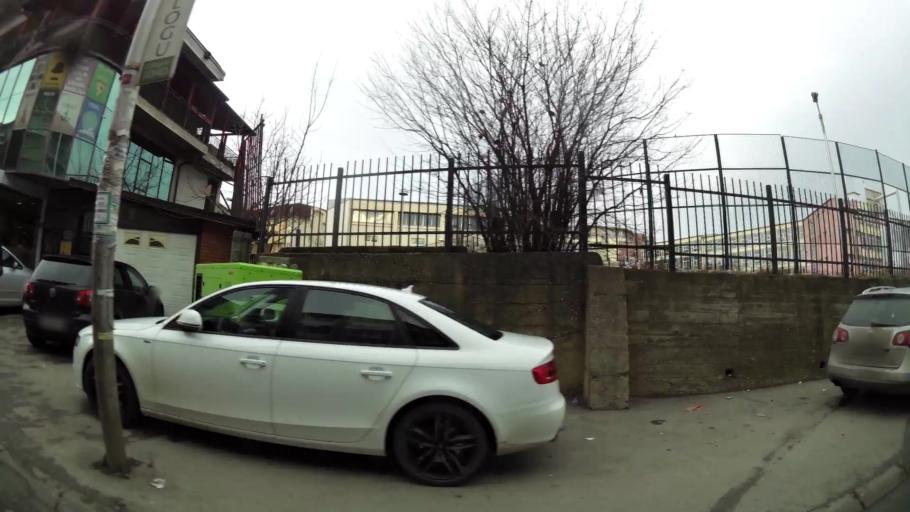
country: XK
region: Pristina
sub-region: Komuna e Prishtines
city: Pristina
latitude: 42.6487
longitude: 21.1598
